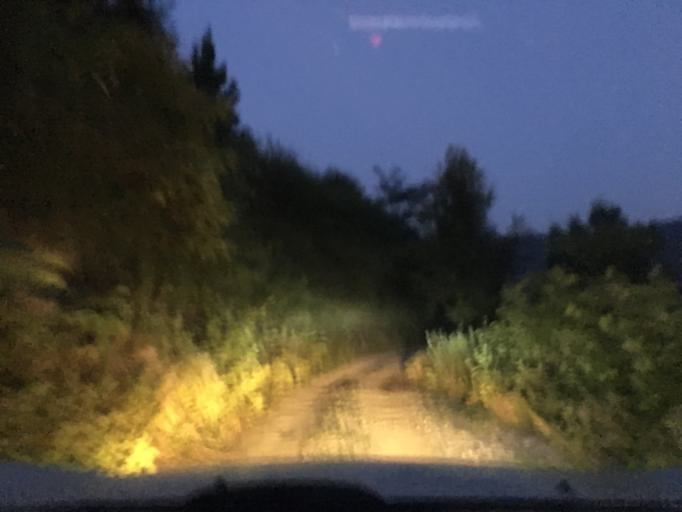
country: CN
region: Guangxi Zhuangzu Zizhiqu
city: Xinzhou
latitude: 25.3548
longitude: 105.7276
